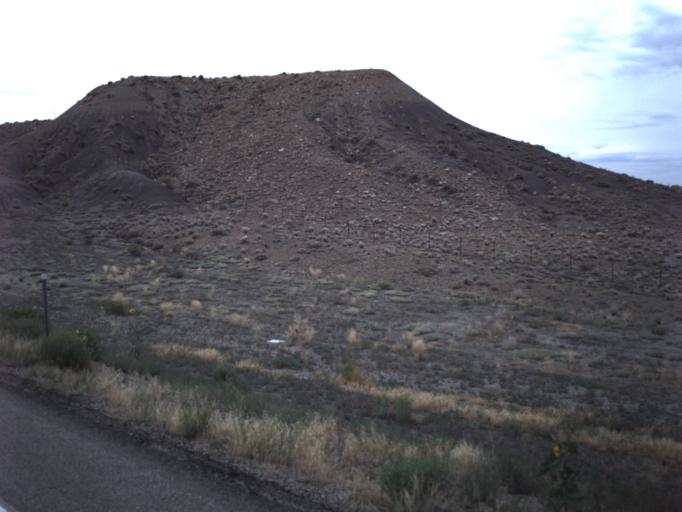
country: US
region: Utah
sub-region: Carbon County
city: East Carbon City
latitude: 39.3446
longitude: -110.3751
